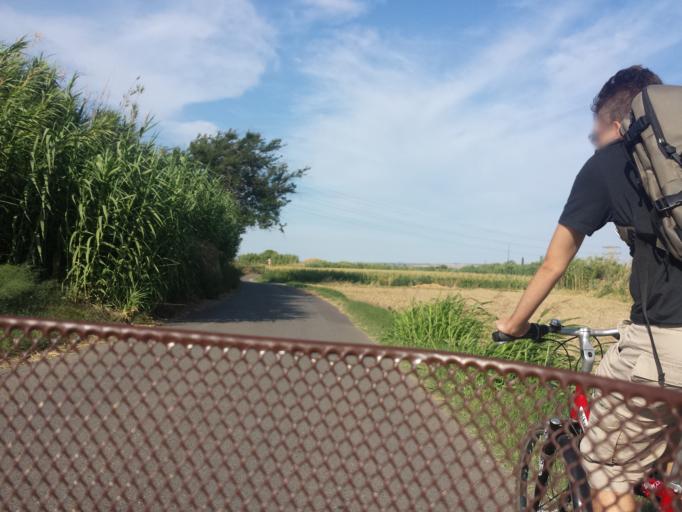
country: ES
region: Aragon
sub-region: Provincia de Zaragoza
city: Zaragoza
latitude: 41.6999
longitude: -0.8573
